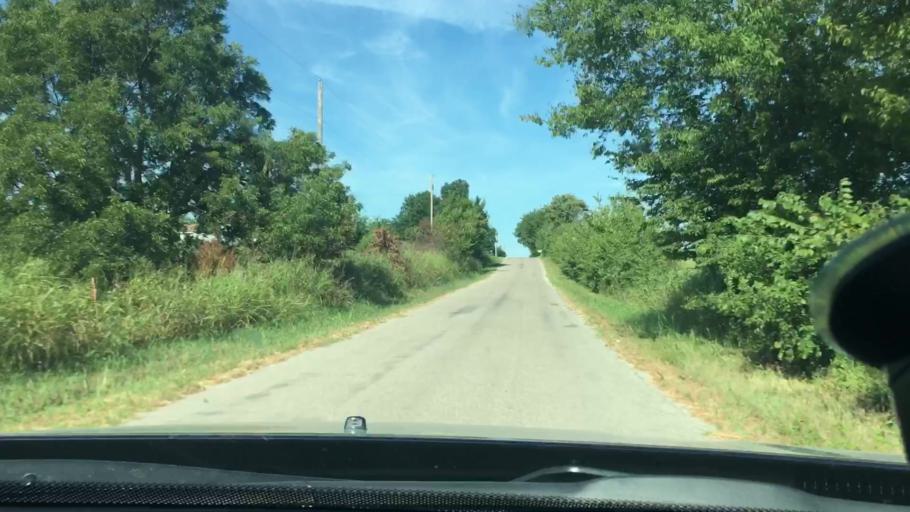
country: US
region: Oklahoma
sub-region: Carter County
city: Lone Grove
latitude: 34.2674
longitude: -97.2611
